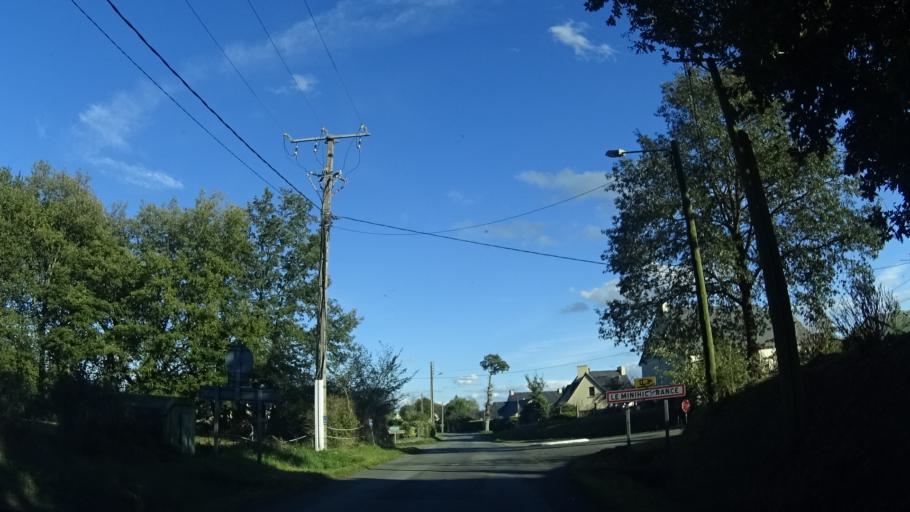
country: FR
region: Brittany
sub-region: Departement d'Ille-et-Vilaine
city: Le Minihic-sur-Rance
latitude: 48.5834
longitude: -2.0124
